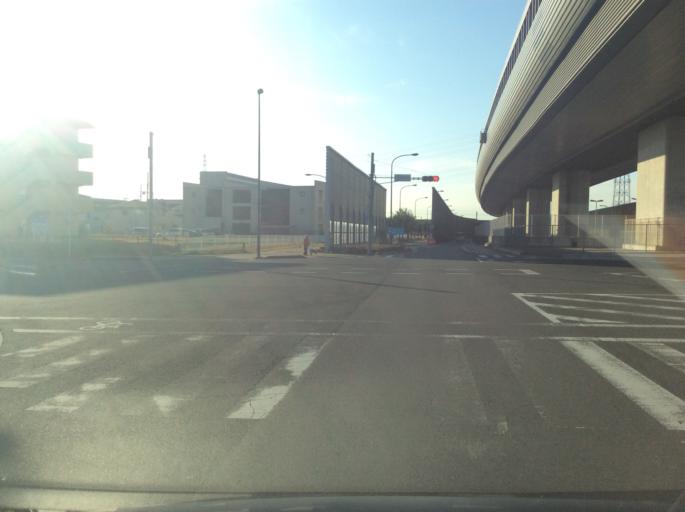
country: JP
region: Saitama
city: Yashio-shi
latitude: 35.8236
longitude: 139.8721
